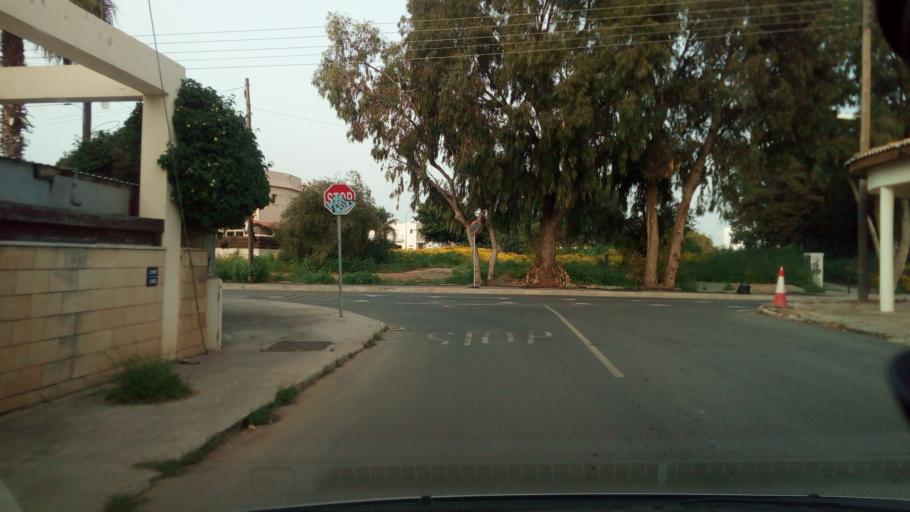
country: CY
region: Limassol
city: Limassol
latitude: 34.6569
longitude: 33.0042
